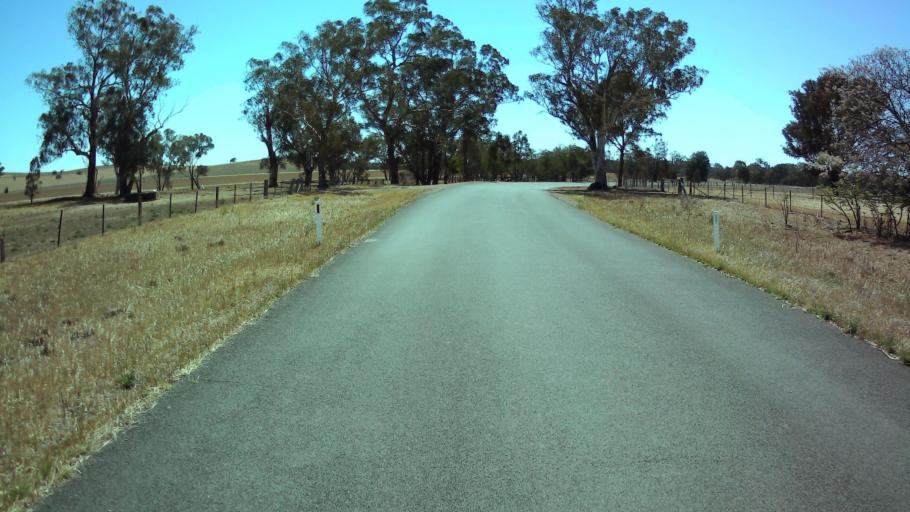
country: AU
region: New South Wales
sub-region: Weddin
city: Grenfell
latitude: -34.0022
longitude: 148.3725
